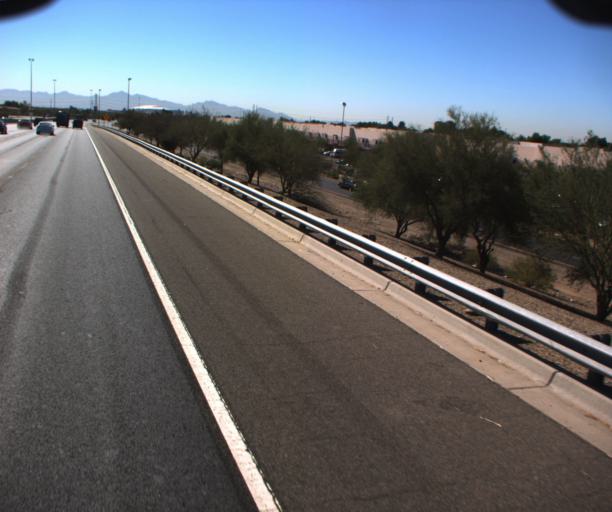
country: US
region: Arizona
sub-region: Maricopa County
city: Peoria
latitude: 33.5654
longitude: -112.2574
